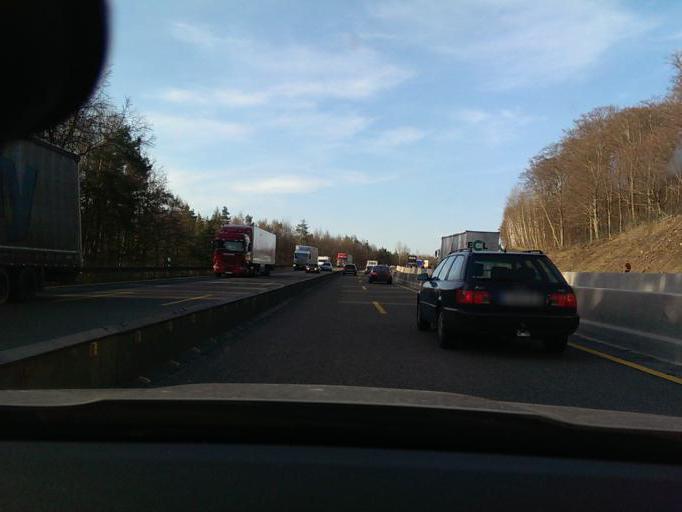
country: DE
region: Hesse
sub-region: Regierungsbezirk Kassel
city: Korle
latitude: 51.1470
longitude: 9.4757
